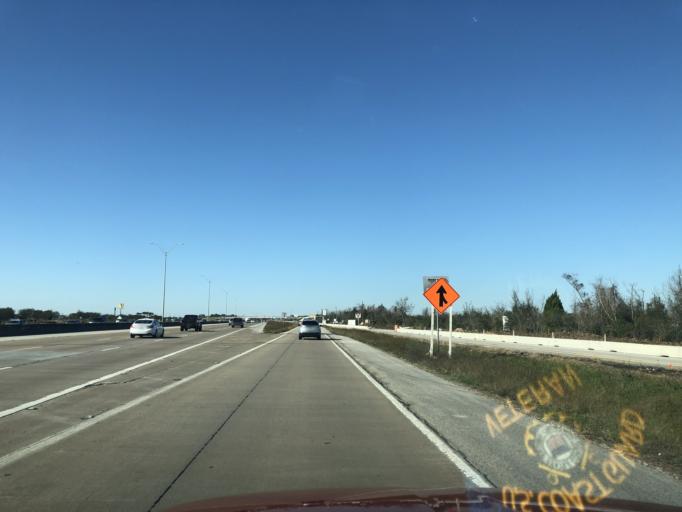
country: US
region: Texas
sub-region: Galveston County
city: Dickinson
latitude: 29.4246
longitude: -95.0543
